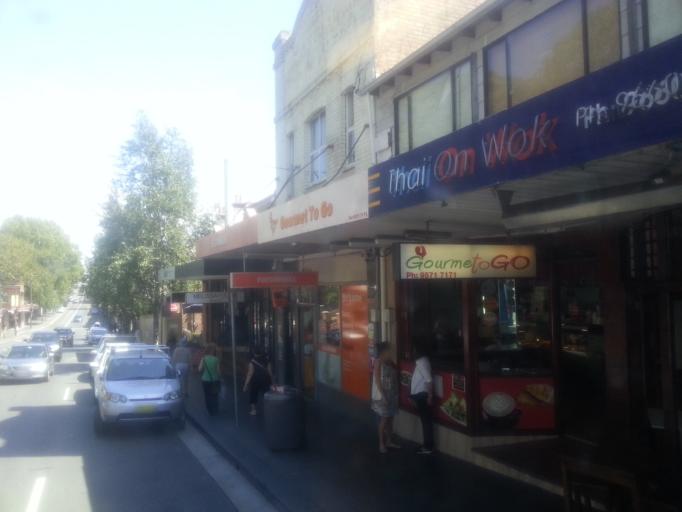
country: AU
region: New South Wales
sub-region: City of Sydney
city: Chippendale
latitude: -33.8805
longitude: 151.1875
